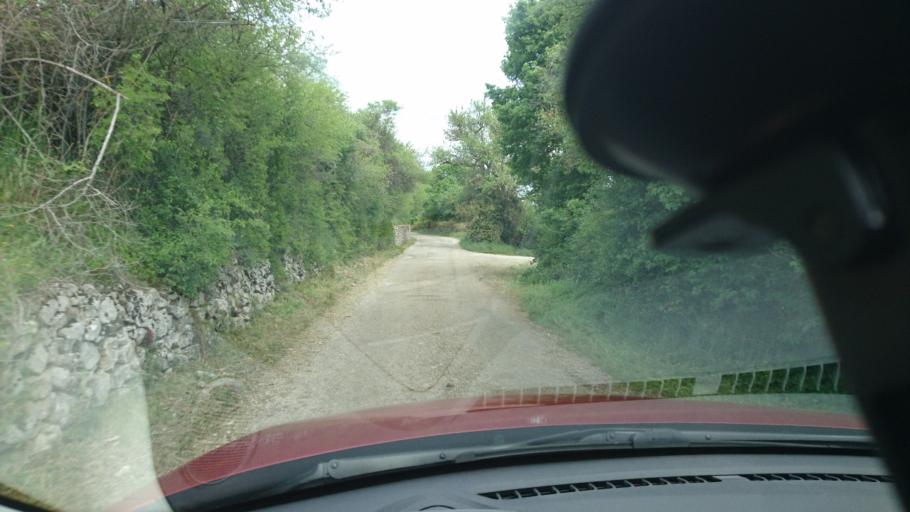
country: FR
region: Provence-Alpes-Cote d'Azur
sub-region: Departement du Vaucluse
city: Sault
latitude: 44.0615
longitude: 5.3580
